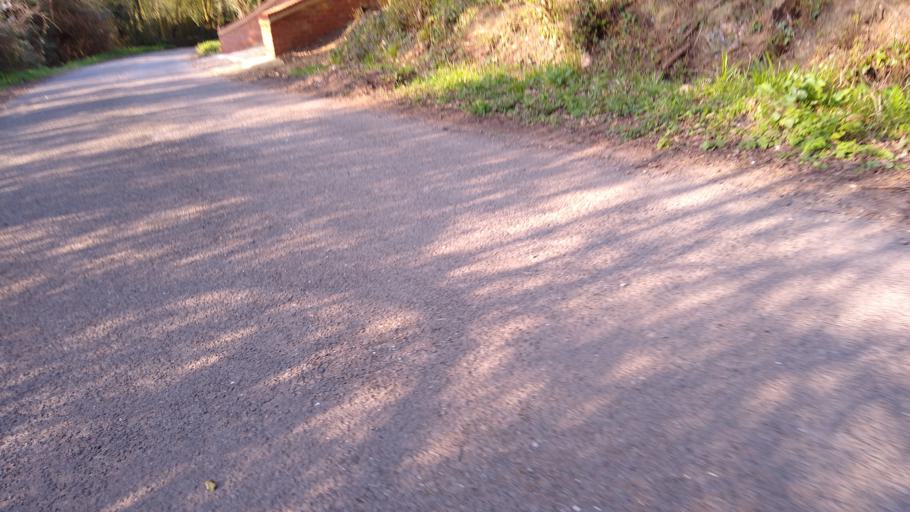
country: GB
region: England
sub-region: Wokingham
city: Winnersh
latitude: 51.4381
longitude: -0.8636
